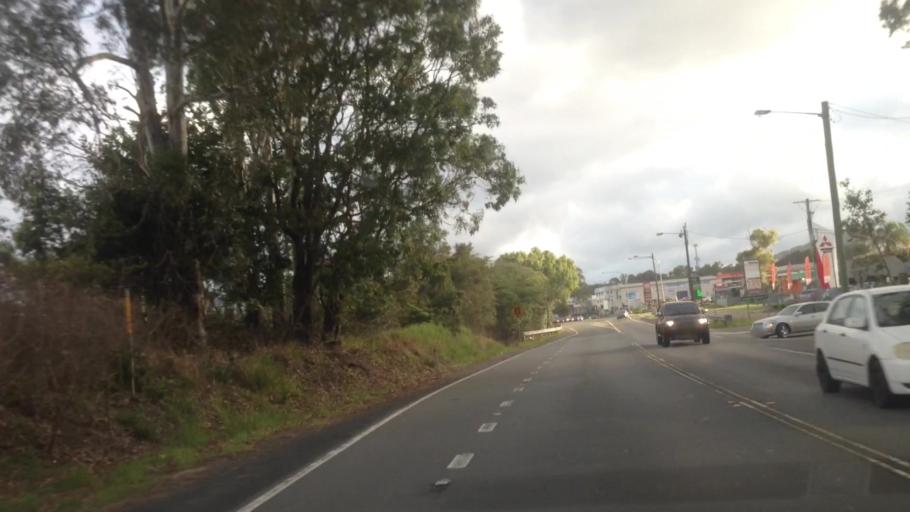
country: AU
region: New South Wales
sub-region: Wyong Shire
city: Chittaway Bay
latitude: -33.2923
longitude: 151.4236
